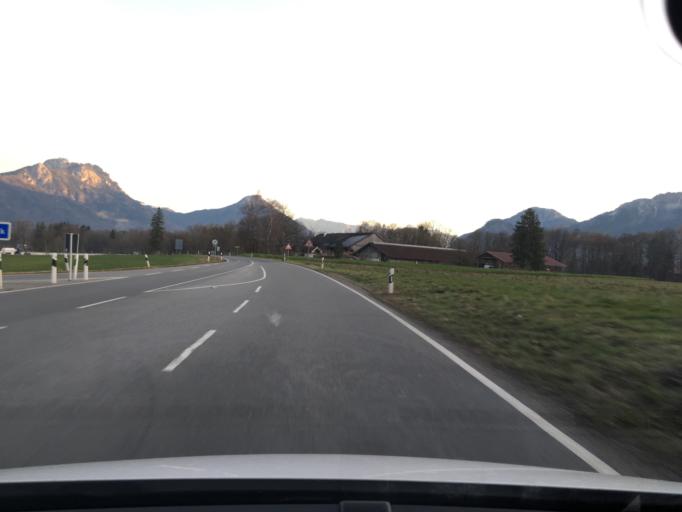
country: DE
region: Bavaria
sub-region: Upper Bavaria
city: Brannenburg
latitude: 47.7589
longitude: 12.1059
